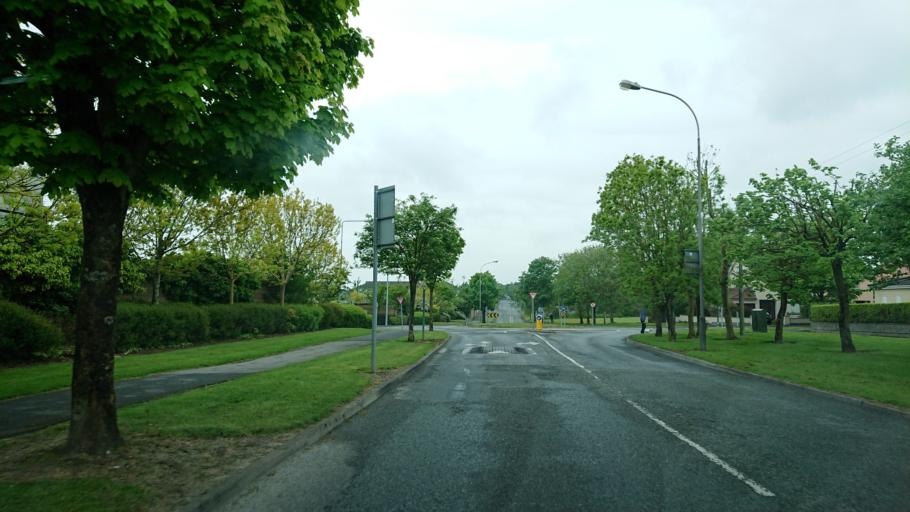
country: IE
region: Munster
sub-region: Waterford
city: Waterford
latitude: 52.2480
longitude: -7.1411
